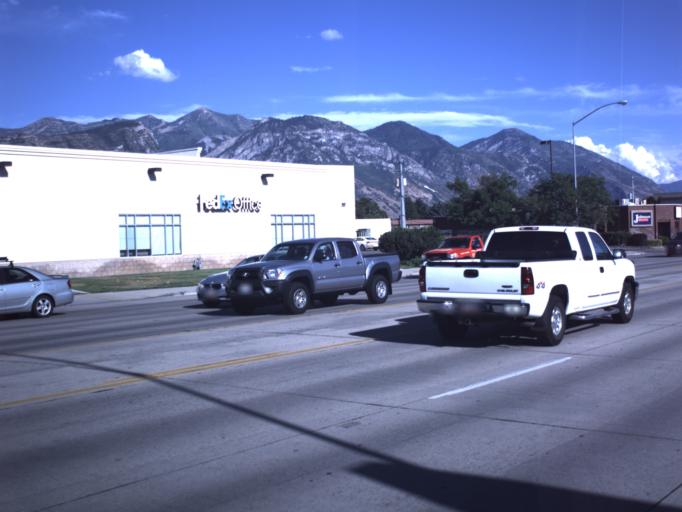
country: US
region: Utah
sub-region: Utah County
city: Orem
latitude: 40.2946
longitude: -111.6940
